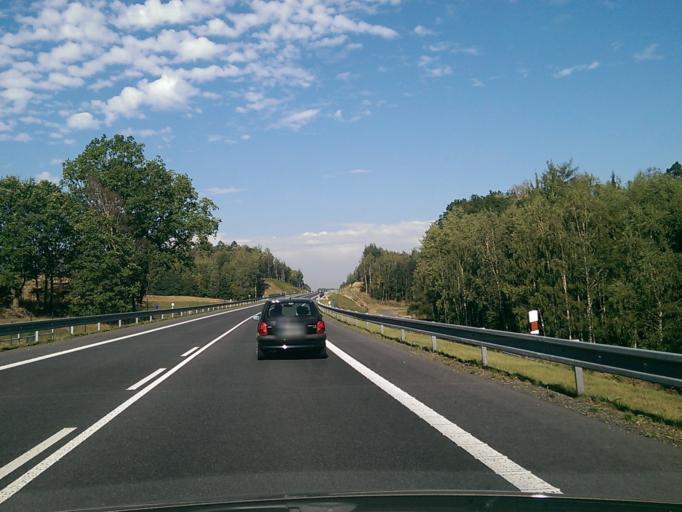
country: CZ
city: Hradek nad Nisou
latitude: 50.8435
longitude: 14.9078
